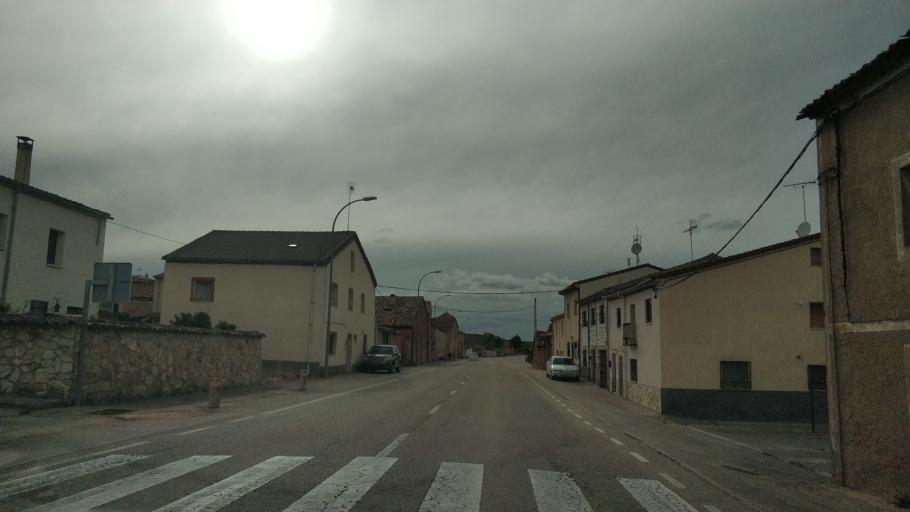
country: ES
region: Castille and Leon
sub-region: Provincia de Soria
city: Valdenebro
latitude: 41.5697
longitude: -3.0089
